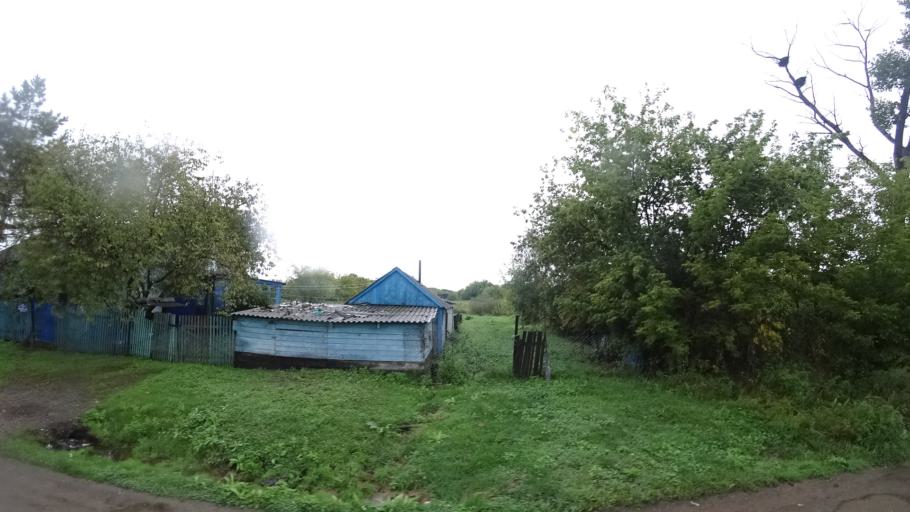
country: RU
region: Primorskiy
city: Monastyrishche
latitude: 44.2550
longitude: 132.4270
